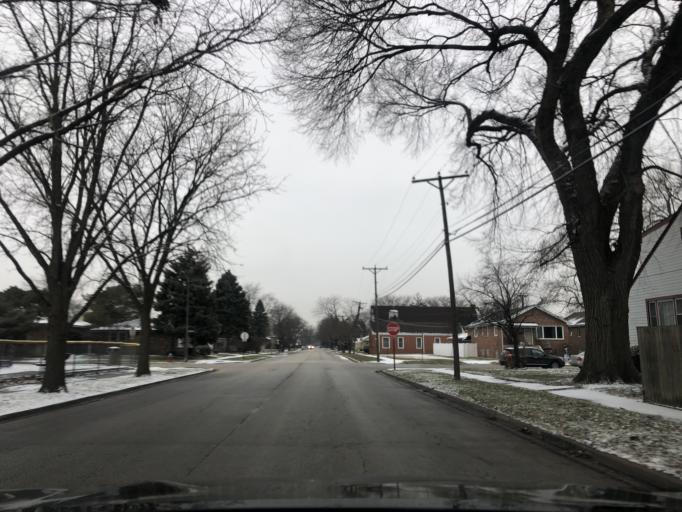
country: US
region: Illinois
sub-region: Cook County
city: Evergreen Park
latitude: 41.7317
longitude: -87.6929
